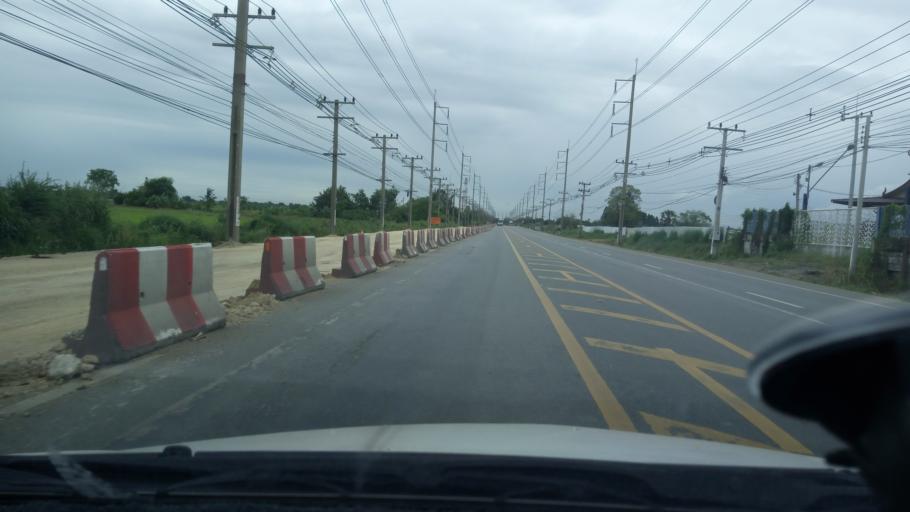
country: TH
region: Chon Buri
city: Phanat Nikhom
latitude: 13.4852
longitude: 101.1671
